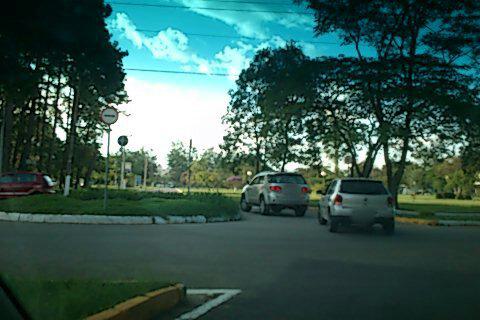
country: BR
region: Sao Paulo
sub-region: Sao Jose Dos Campos
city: Sao Jose dos Campos
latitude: -23.2062
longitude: -45.8763
